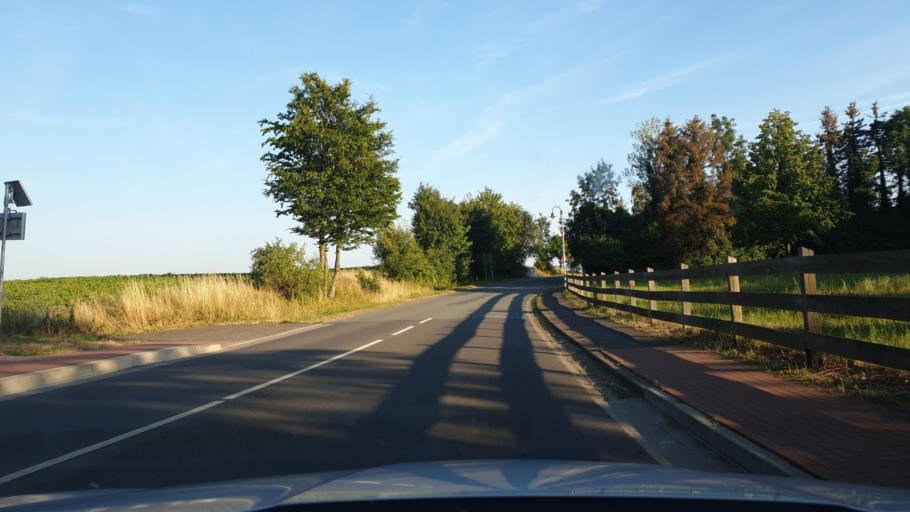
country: DE
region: Lower Saxony
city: Heuerssen
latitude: 52.2923
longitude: 9.2908
